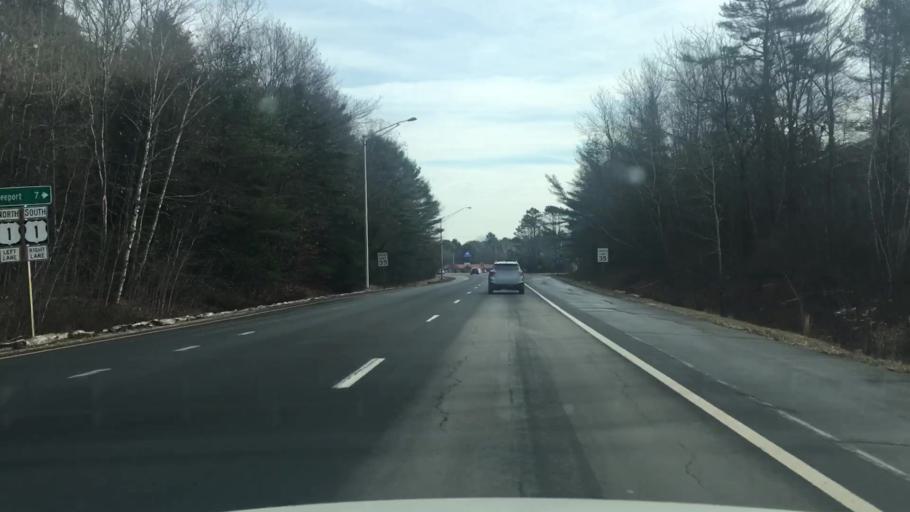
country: US
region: Maine
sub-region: Sagadahoc County
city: Topsham
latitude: 43.9132
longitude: -70.0041
